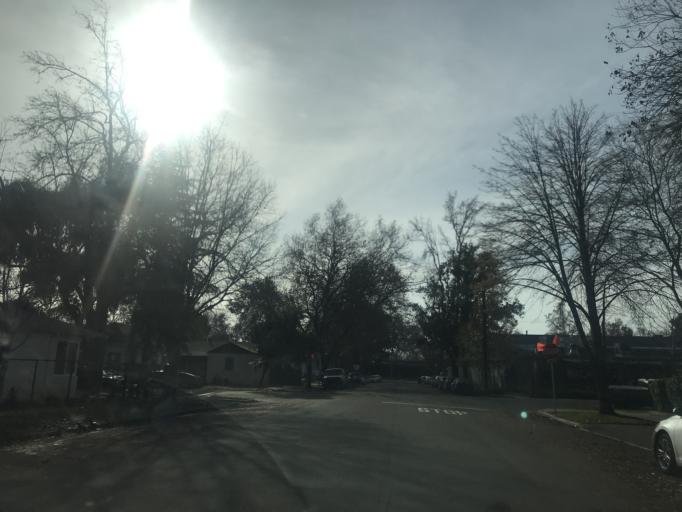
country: US
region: California
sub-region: Sacramento County
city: Sacramento
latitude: 38.5660
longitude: -121.4935
